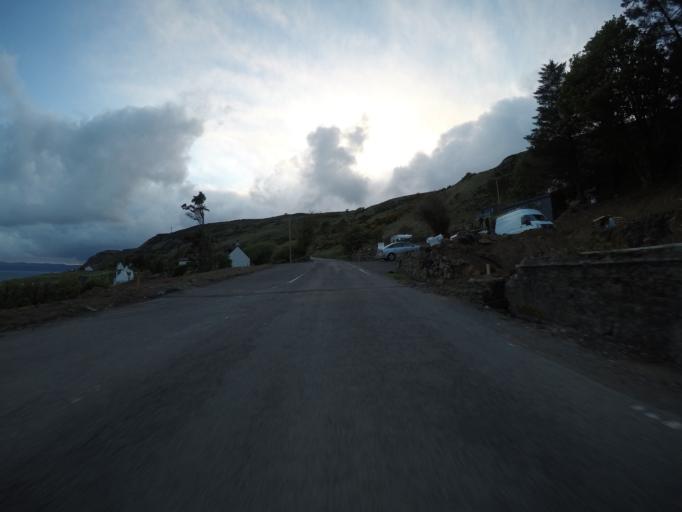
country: GB
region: Scotland
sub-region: Highland
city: Portree
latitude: 57.5922
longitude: -6.3708
